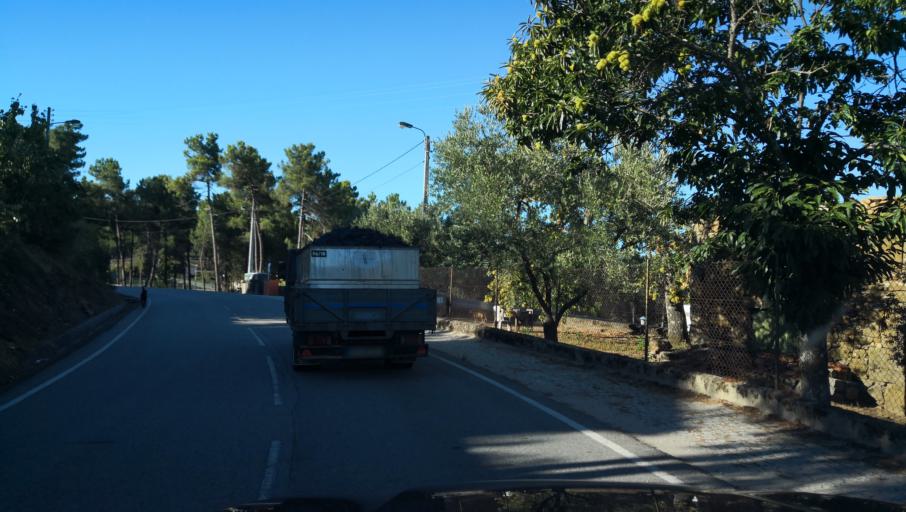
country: PT
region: Vila Real
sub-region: Sabrosa
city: Sabrosa
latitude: 41.2955
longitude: -7.5787
